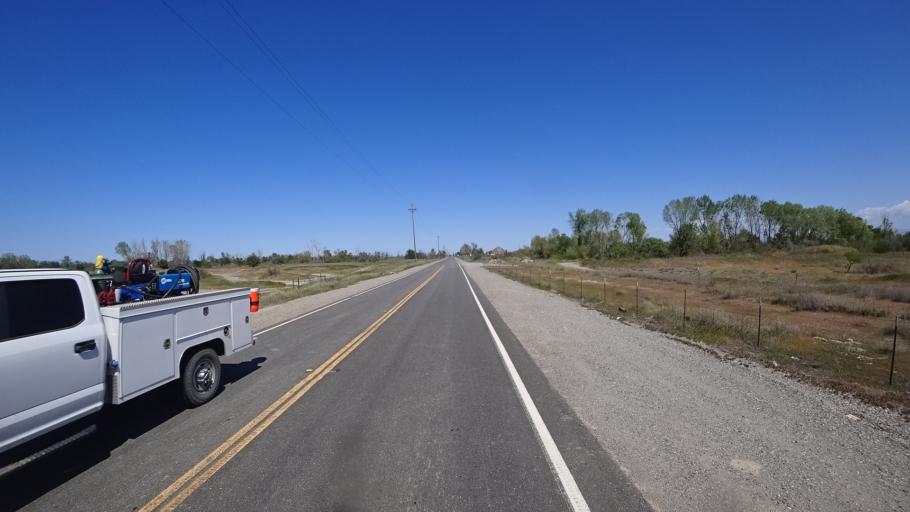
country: US
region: California
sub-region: Glenn County
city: Orland
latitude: 39.7606
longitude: -122.1409
